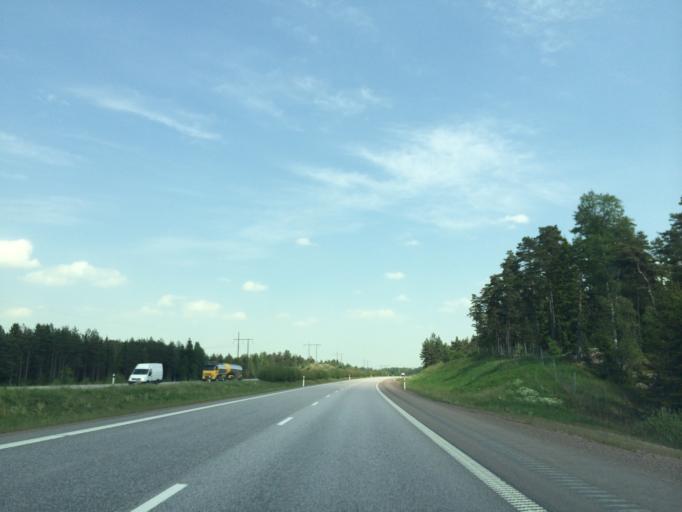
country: SE
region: OEstergoetland
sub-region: Vadstena Kommun
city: Herrestad
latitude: 58.2617
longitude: 14.8390
